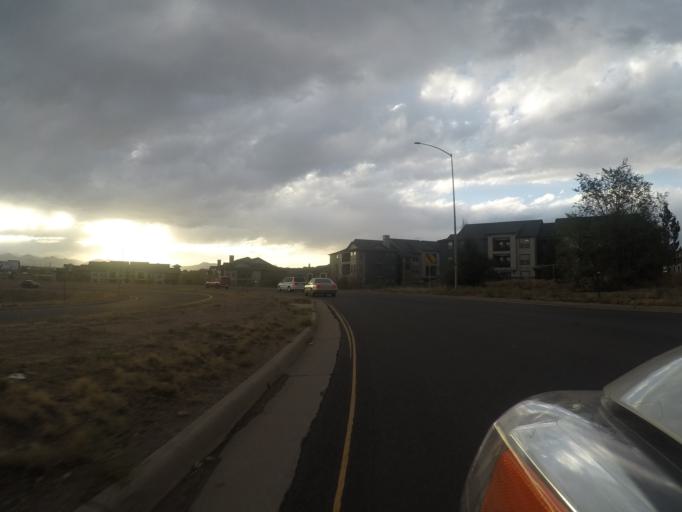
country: US
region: Colorado
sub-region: Arapahoe County
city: Englewood
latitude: 39.6544
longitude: -105.0024
